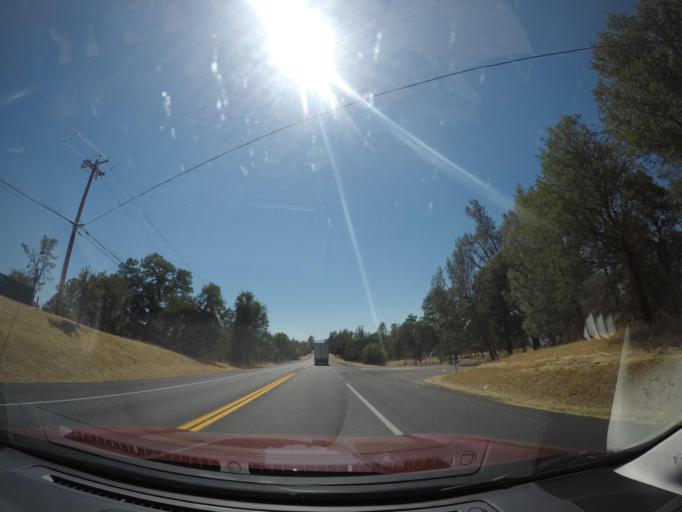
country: US
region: California
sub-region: Shasta County
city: Bella Vista
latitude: 40.6302
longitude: -122.2753
